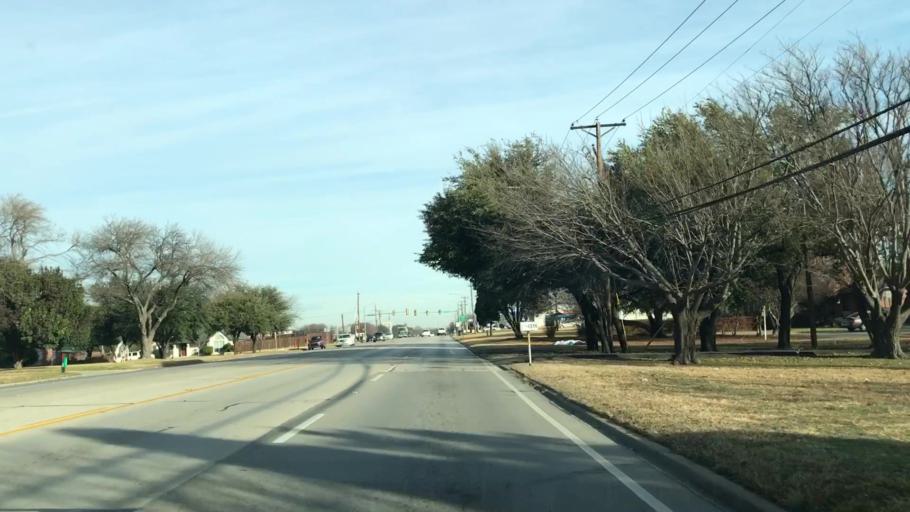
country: US
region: Texas
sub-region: Tarrant County
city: Sansom Park
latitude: 32.8199
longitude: -97.4199
